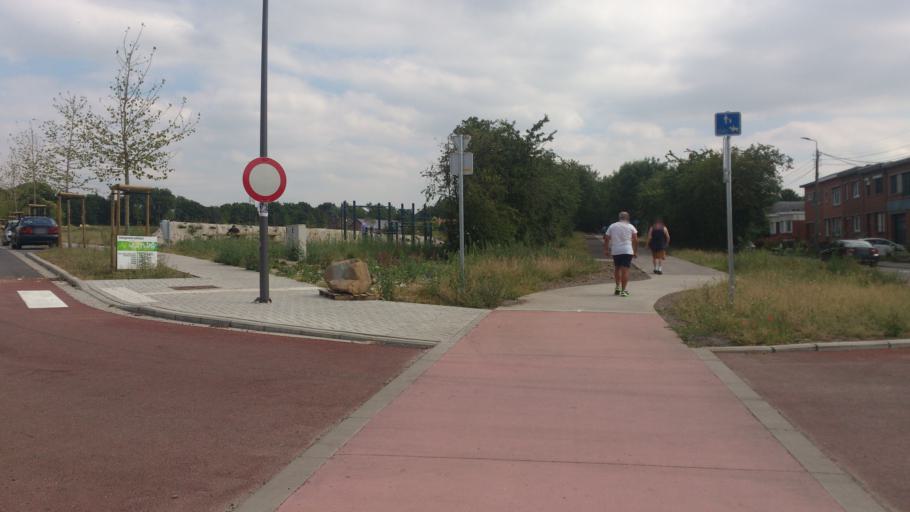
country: BE
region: Wallonia
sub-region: Province de Liege
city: Beyne-Heusay
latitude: 50.6305
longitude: 5.6332
